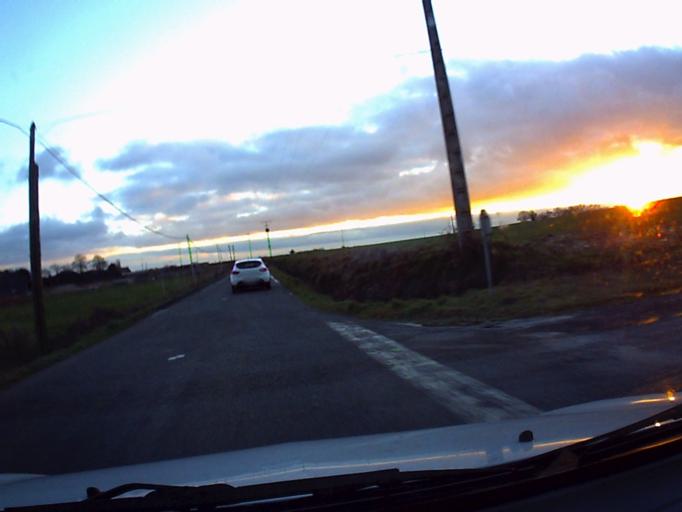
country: FR
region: Brittany
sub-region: Departement d'Ille-et-Vilaine
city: Iffendic
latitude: 48.1450
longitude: -2.0171
